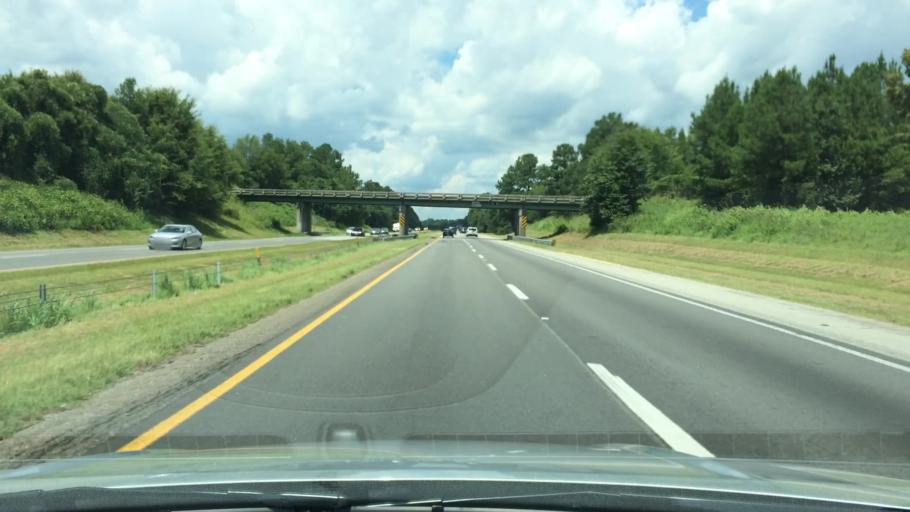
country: US
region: South Carolina
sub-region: Newberry County
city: Prosperity
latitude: 34.2684
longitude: -81.5083
